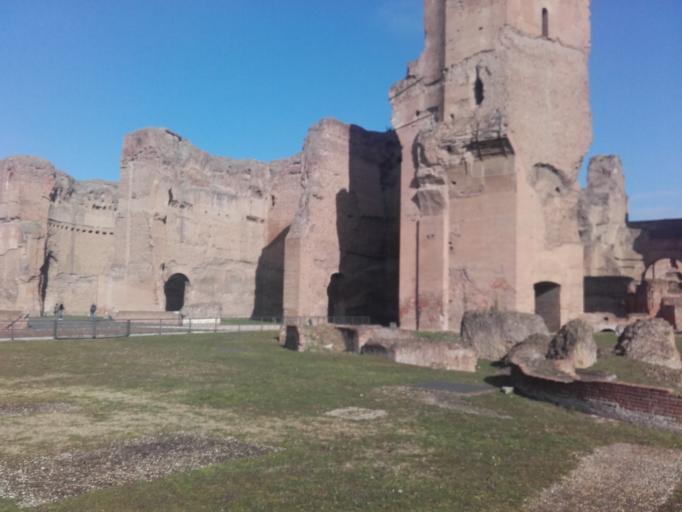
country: IT
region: Latium
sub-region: Citta metropolitana di Roma Capitale
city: Rome
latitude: 41.8787
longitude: 12.4923
